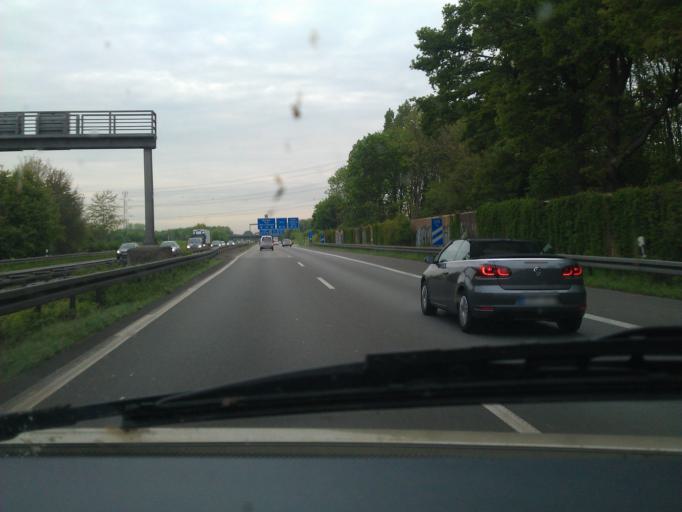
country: DE
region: North Rhine-Westphalia
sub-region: Regierungsbezirk Dusseldorf
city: Moers
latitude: 51.4264
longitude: 6.6054
